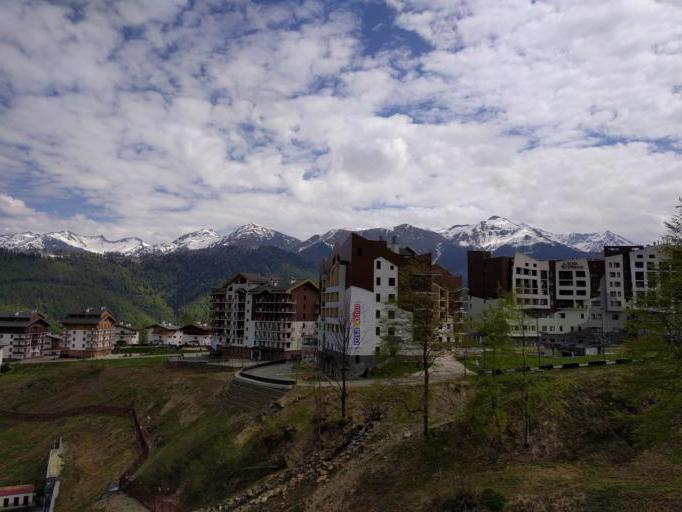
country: RU
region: Krasnodarskiy
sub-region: Sochi City
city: Krasnaya Polyana
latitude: 43.6601
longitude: 40.3165
